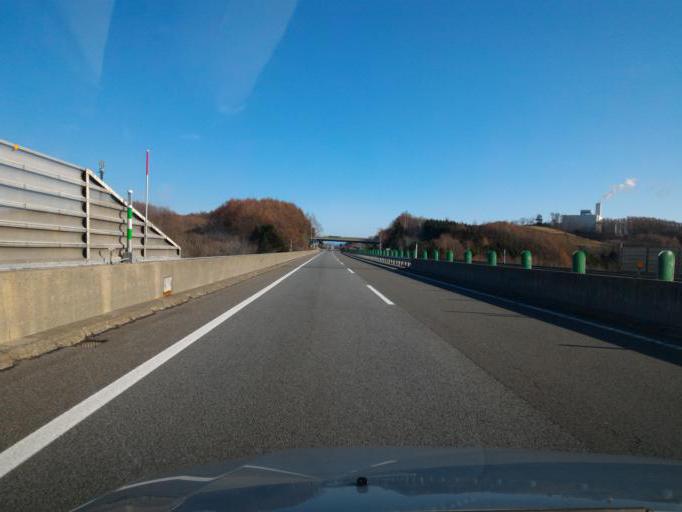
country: JP
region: Hokkaido
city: Iwamizawa
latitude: 43.1894
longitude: 141.7927
